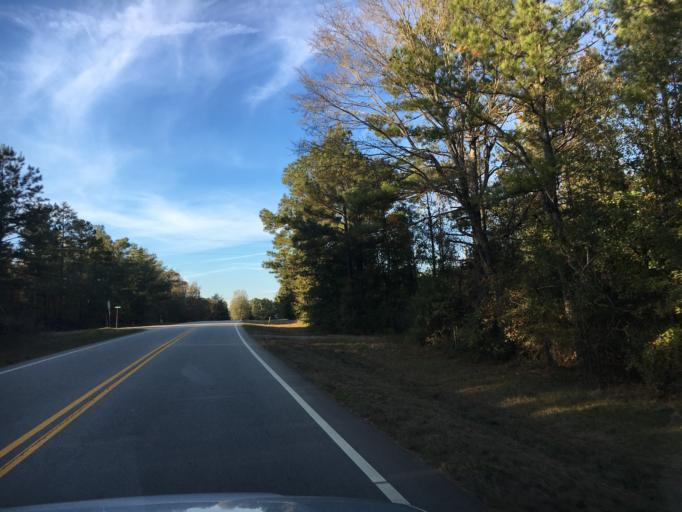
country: US
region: Georgia
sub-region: Elbert County
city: Elberton
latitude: 33.9387
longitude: -82.7671
